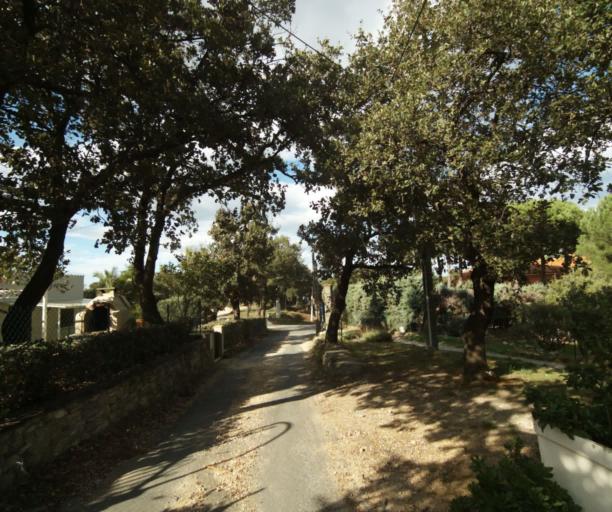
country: FR
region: Languedoc-Roussillon
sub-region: Departement des Pyrenees-Orientales
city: Argelers
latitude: 42.5309
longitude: 3.0261
